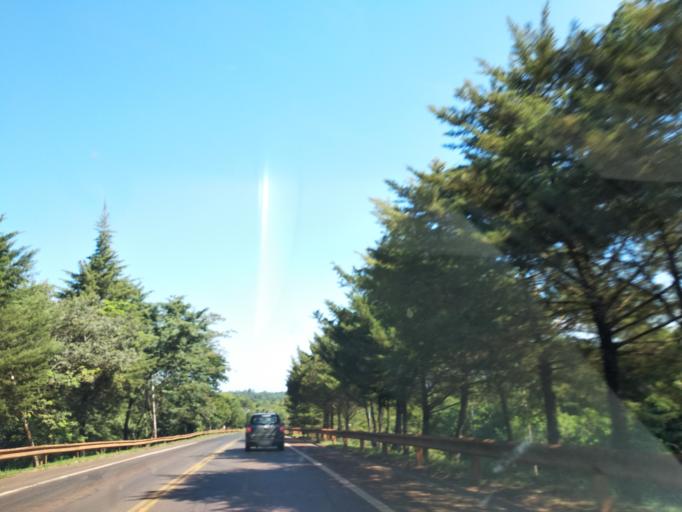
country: AR
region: Misiones
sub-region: Departamento de Eldorado
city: Eldorado
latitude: -26.4042
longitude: -54.6352
